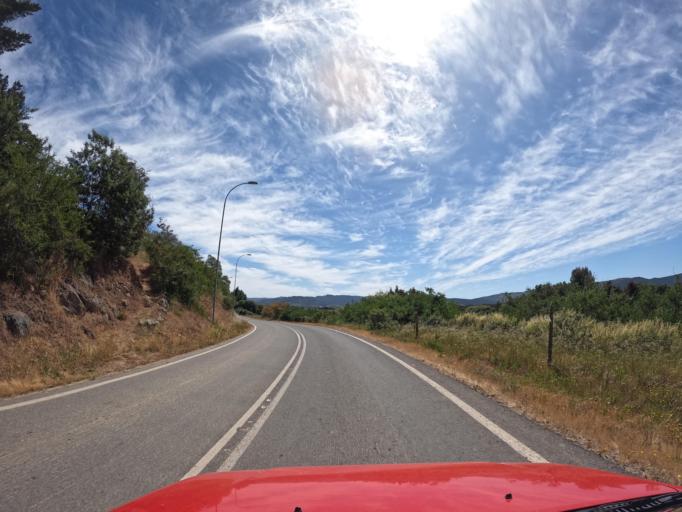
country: CL
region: Maule
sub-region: Provincia de Talca
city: Talca
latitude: -34.9894
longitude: -71.8121
